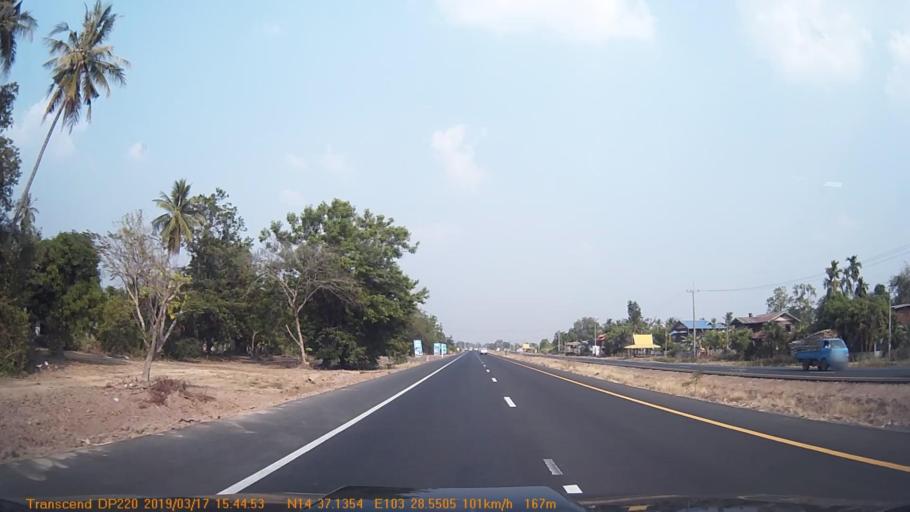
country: TH
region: Surin
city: Prasat
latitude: 14.6189
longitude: 103.4762
